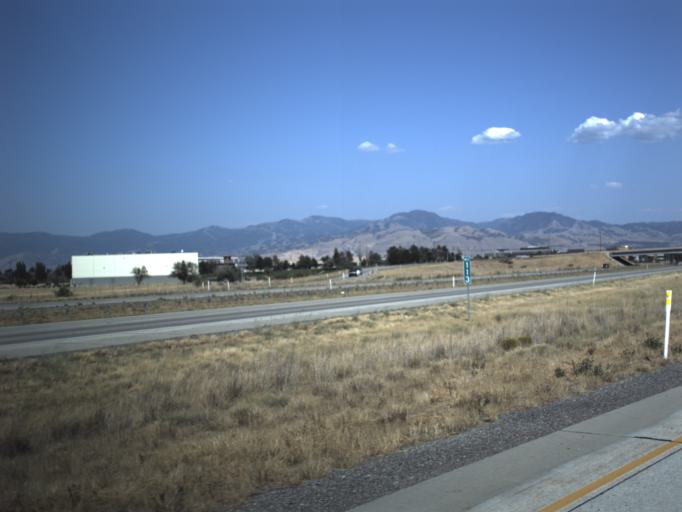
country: US
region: Utah
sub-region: Salt Lake County
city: West Valley City
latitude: 40.7707
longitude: -112.0308
